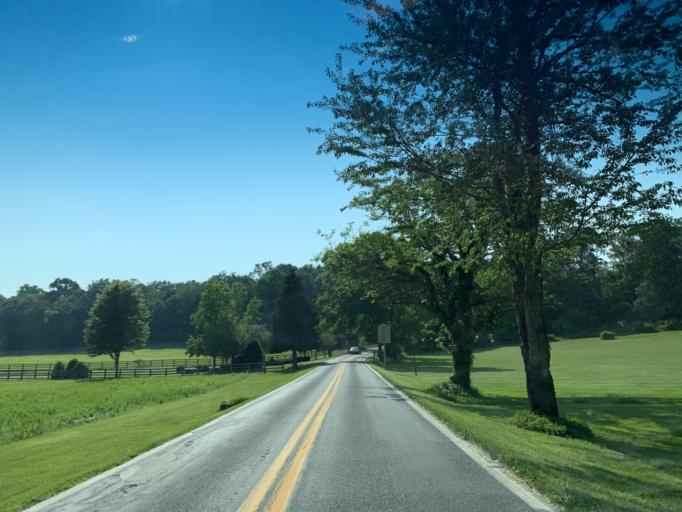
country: US
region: Maryland
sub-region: Frederick County
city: Urbana
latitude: 39.2507
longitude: -77.3803
